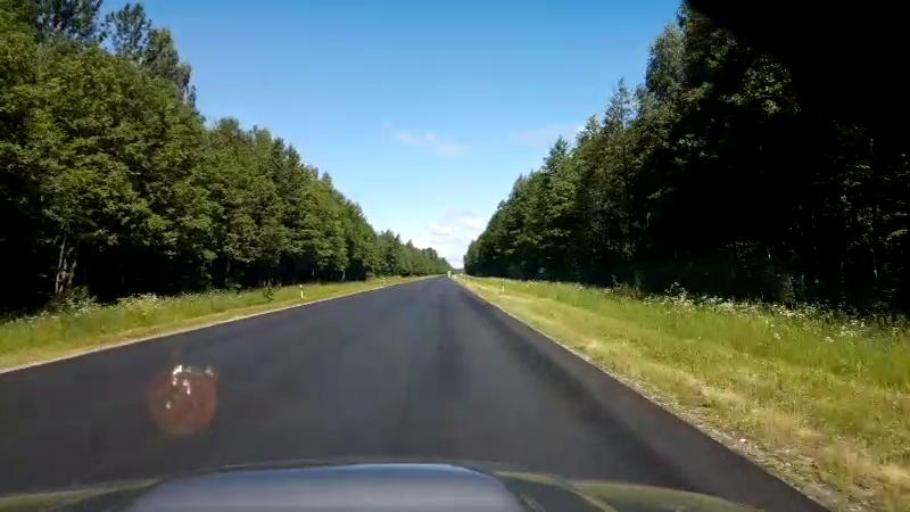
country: LV
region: Salacgrivas
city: Ainazi
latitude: 57.9469
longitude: 24.4348
